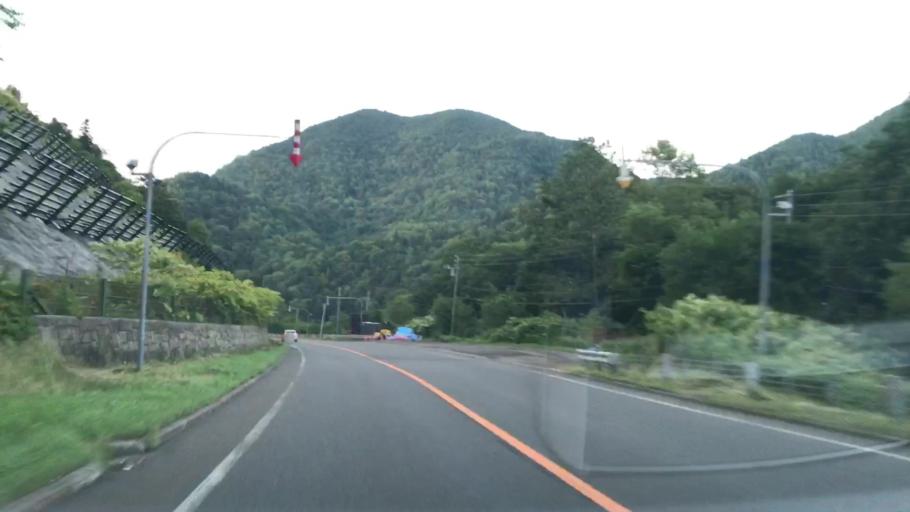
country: JP
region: Hokkaido
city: Sapporo
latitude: 42.9154
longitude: 141.1238
